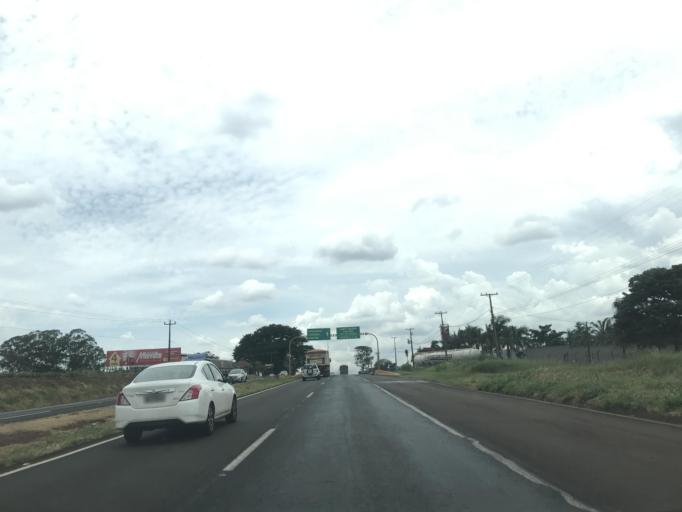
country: BR
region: Parana
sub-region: Maringa
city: Maringa
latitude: -23.3982
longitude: -52.0035
